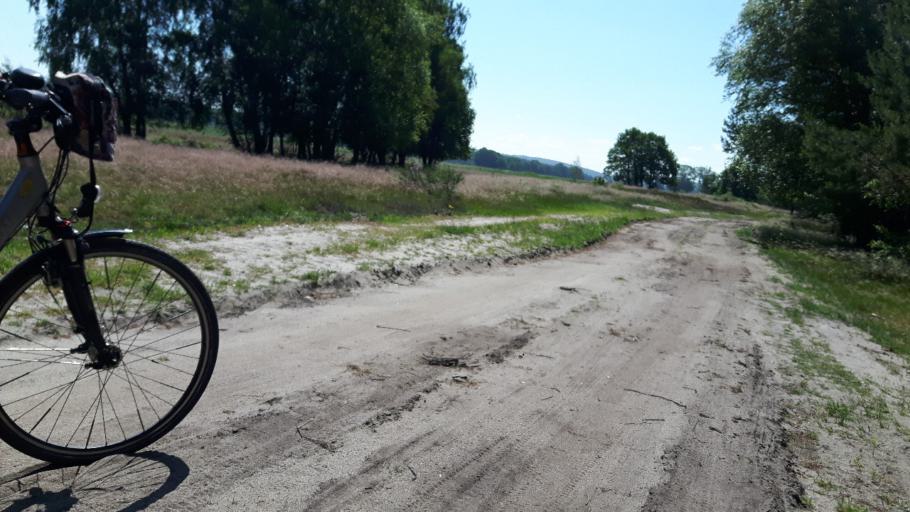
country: PL
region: Pomeranian Voivodeship
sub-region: Powiat slupski
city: Smoldzino
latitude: 54.6745
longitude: 17.1577
